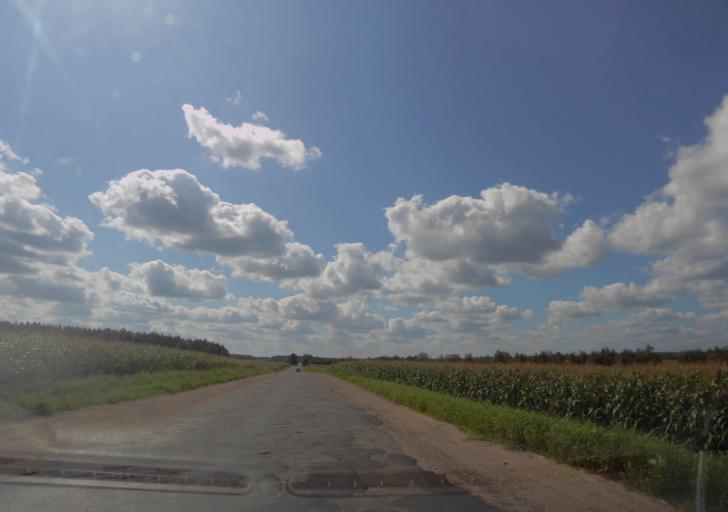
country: BY
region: Minsk
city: Horad Barysaw
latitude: 54.3741
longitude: 28.4750
